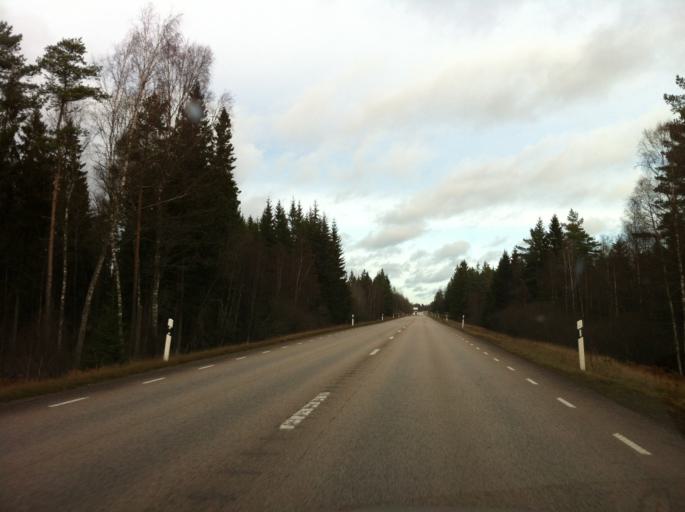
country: SE
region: Kronoberg
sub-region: Uppvidinge Kommun
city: Lenhovda
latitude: 57.1171
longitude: 15.2227
